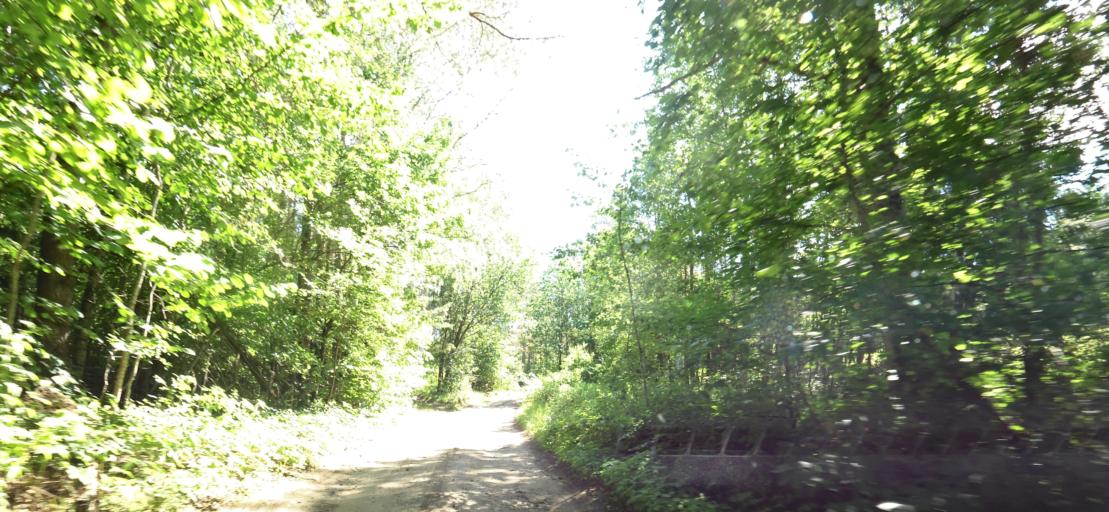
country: LT
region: Vilnius County
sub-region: Vilnius
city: Fabijoniskes
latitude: 54.8293
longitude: 25.3227
